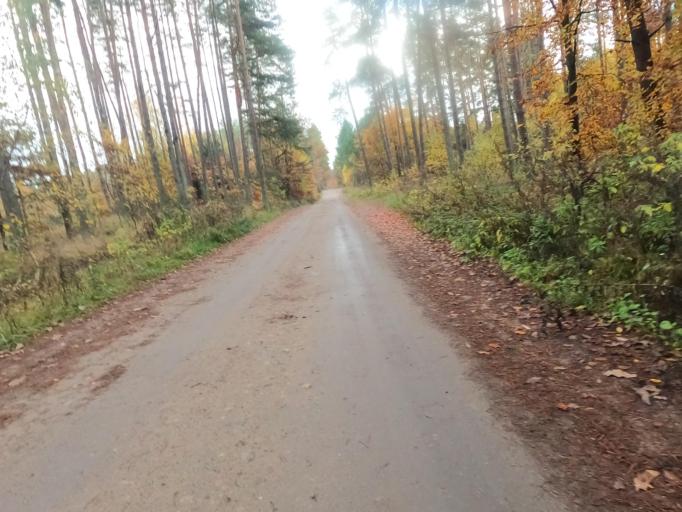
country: PL
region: West Pomeranian Voivodeship
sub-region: Powiat szczecinecki
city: Lubowo
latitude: 53.5345
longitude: 16.4519
